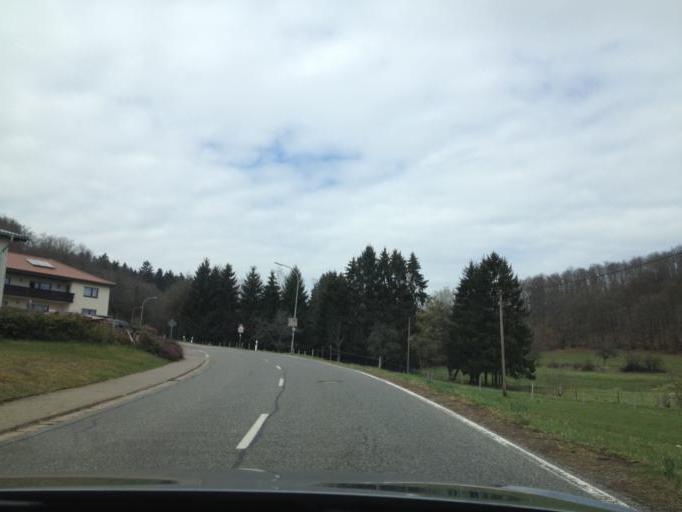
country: DE
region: Saarland
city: Freisen
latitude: 49.5573
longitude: 7.2449
